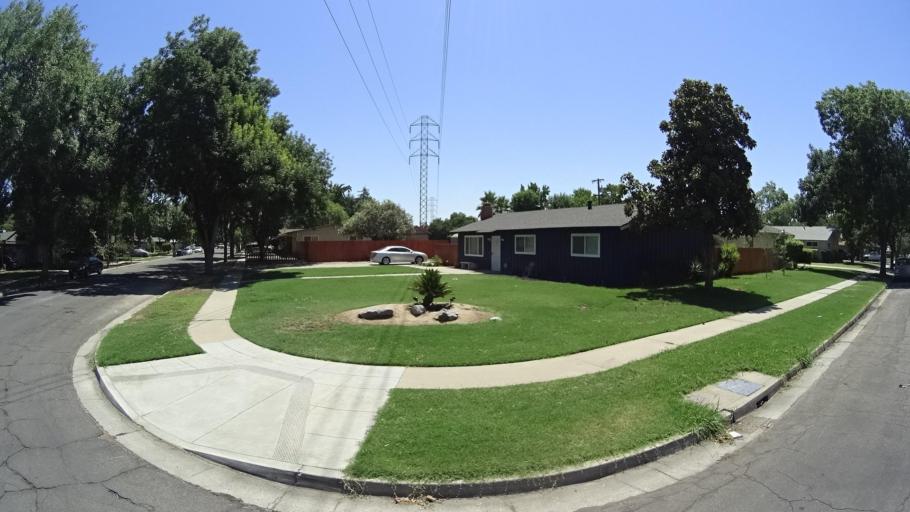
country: US
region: California
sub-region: Fresno County
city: Fresno
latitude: 36.7849
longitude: -119.7787
